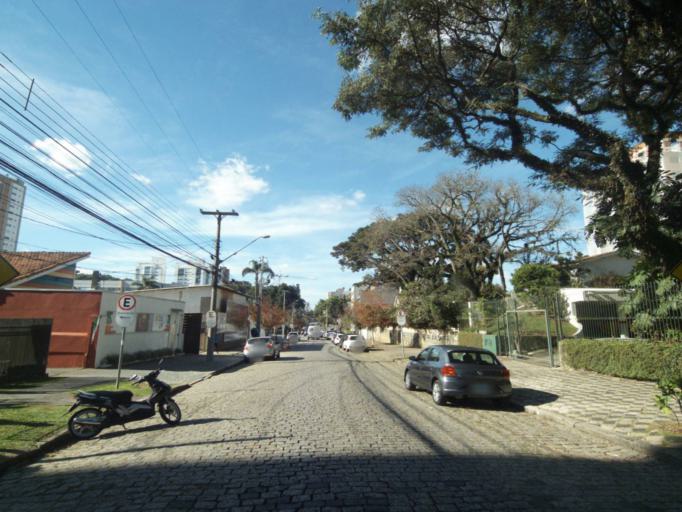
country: BR
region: Parana
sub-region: Curitiba
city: Curitiba
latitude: -25.4354
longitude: -49.2895
